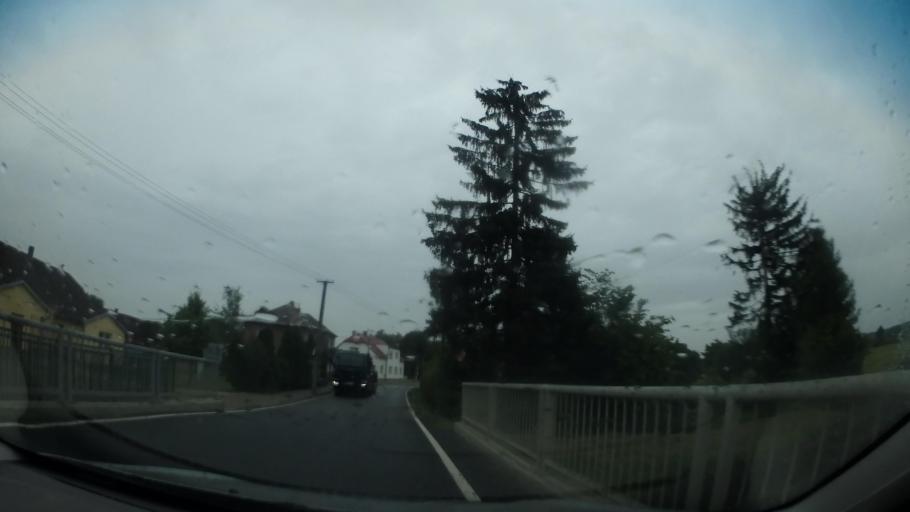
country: CZ
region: Central Bohemia
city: Milovice
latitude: 50.2354
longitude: 14.9602
